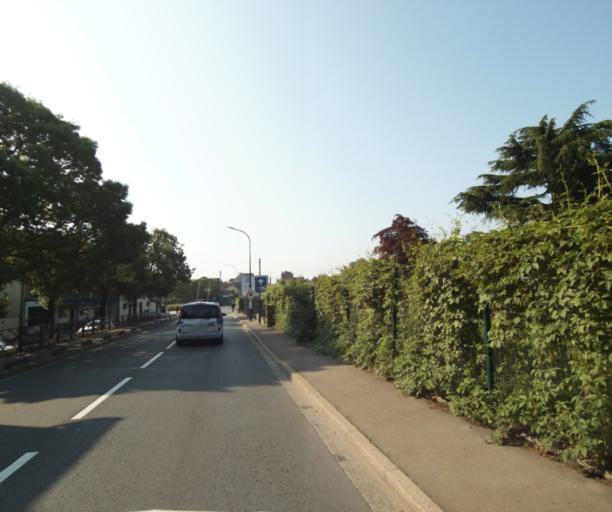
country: FR
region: Ile-de-France
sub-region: Departement du Val-d'Oise
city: Argenteuil
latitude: 48.9536
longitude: 2.2431
